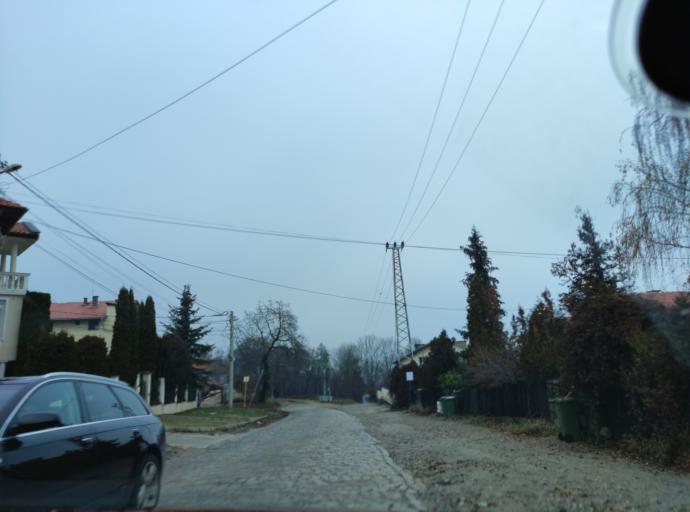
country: BG
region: Sofia-Capital
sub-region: Stolichna Obshtina
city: Sofia
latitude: 42.6249
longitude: 23.3085
